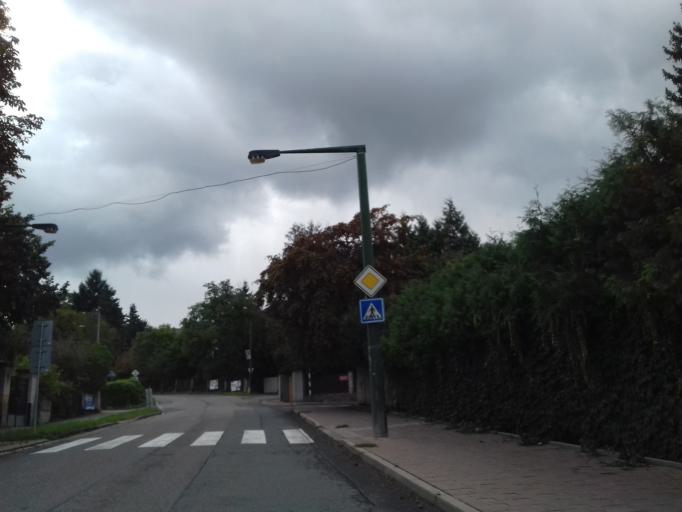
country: CZ
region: Central Bohemia
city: Cernosice
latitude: 49.9580
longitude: 14.3221
